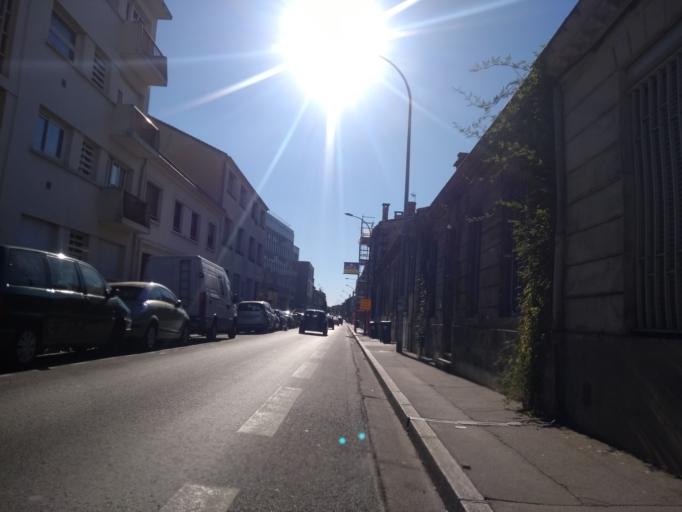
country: FR
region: Aquitaine
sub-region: Departement de la Gironde
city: Bordeaux
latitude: 44.8245
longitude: -0.5642
